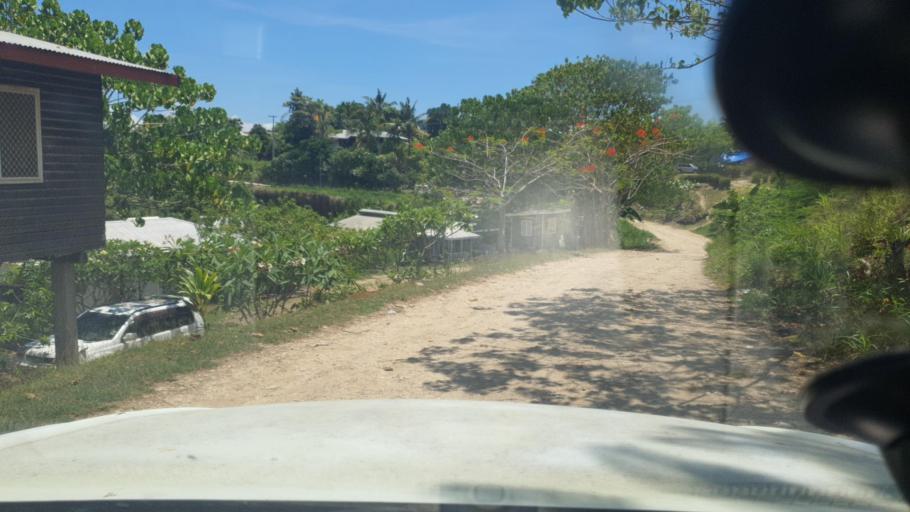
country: SB
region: Guadalcanal
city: Honiara
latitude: -9.4322
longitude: 159.9329
